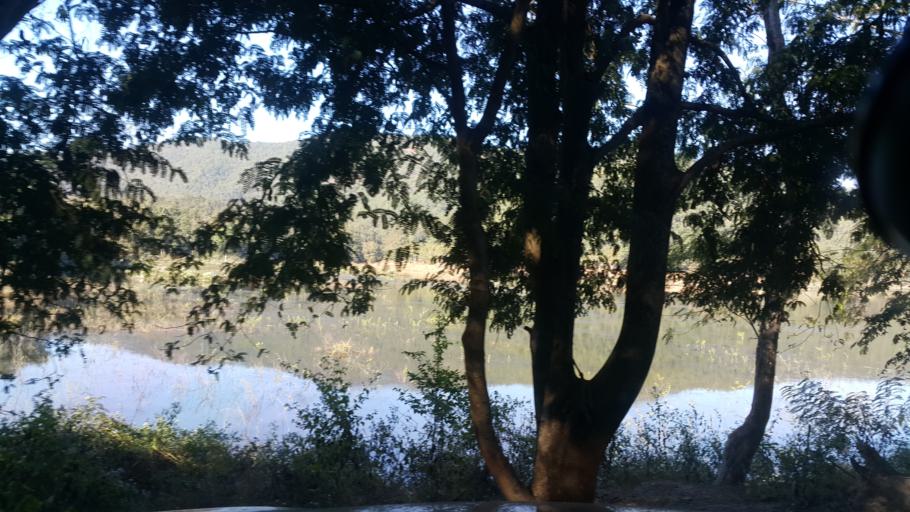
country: TH
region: Chiang Mai
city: Mae On
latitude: 18.6981
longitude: 99.2053
